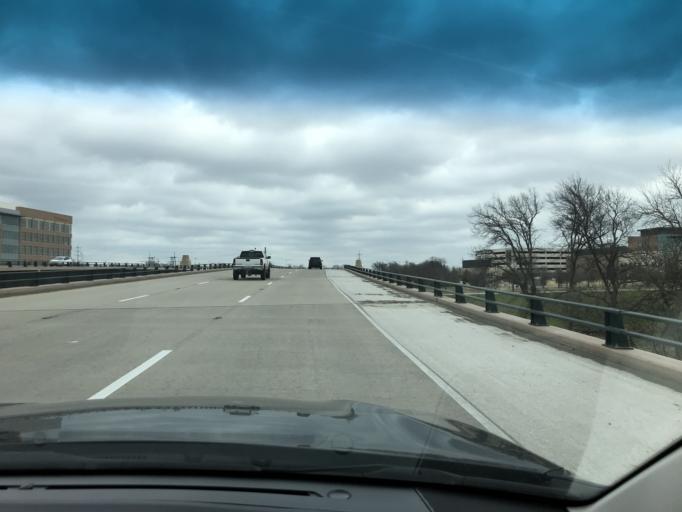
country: US
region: Texas
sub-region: Tarrant County
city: Westworth
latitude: 32.7053
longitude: -97.4052
